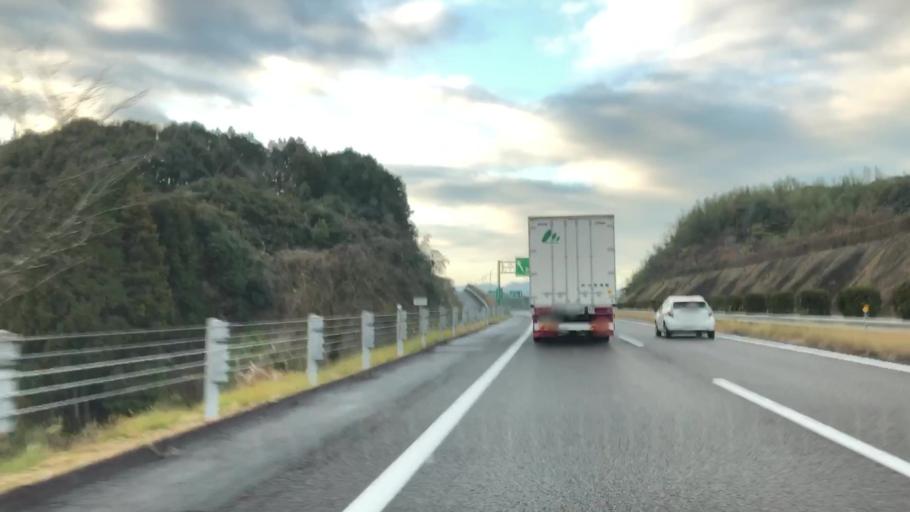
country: JP
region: Saga Prefecture
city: Ureshinomachi-shimojuku
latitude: 33.1517
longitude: 130.0007
